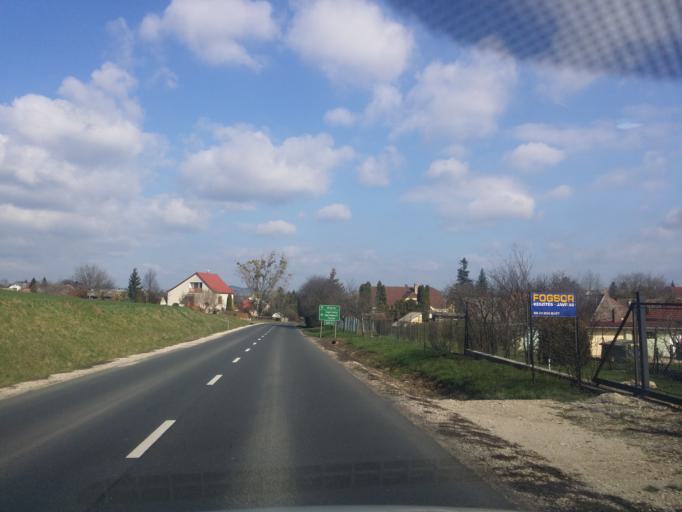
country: HU
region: Fejer
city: Many
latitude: 47.5885
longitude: 18.6658
